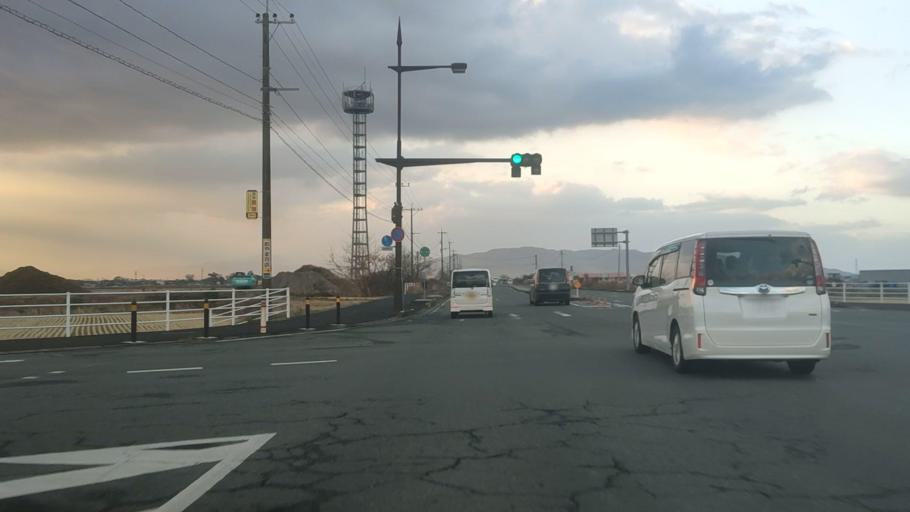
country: JP
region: Kumamoto
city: Kumamoto
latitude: 32.7572
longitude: 130.7061
